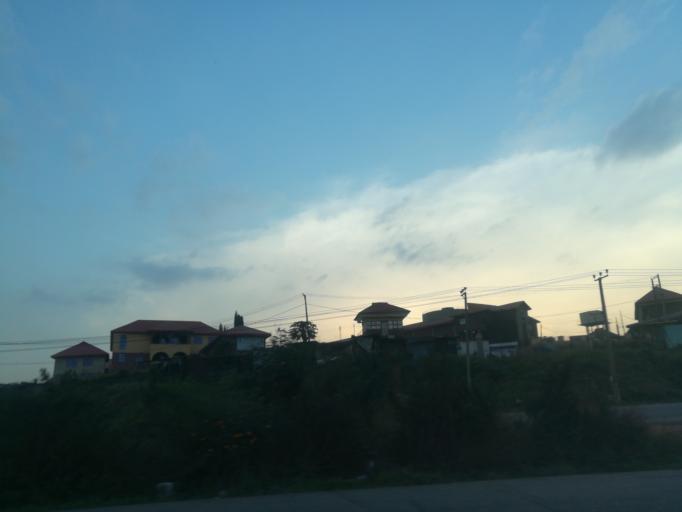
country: NG
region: Oyo
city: Ibadan
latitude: 7.4367
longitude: 3.9320
